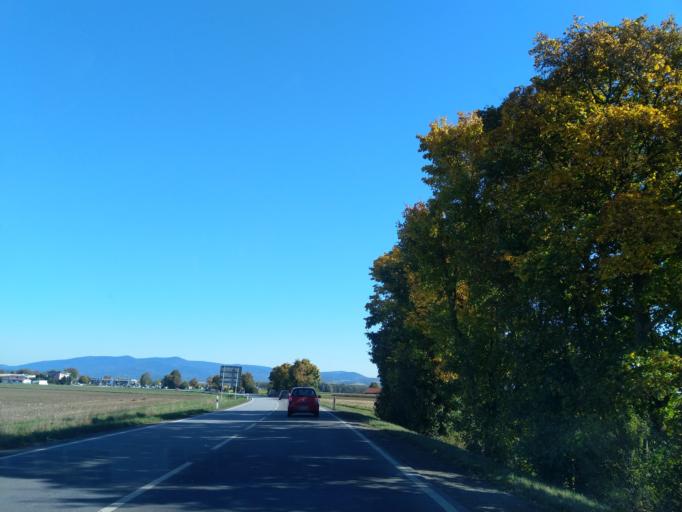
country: DE
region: Bavaria
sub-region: Lower Bavaria
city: Plattling
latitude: 48.7898
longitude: 12.9011
